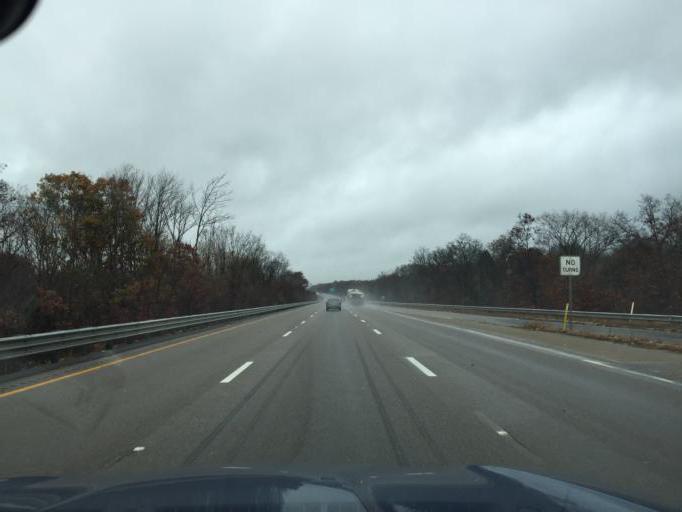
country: US
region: Massachusetts
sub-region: Bristol County
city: Attleboro
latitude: 41.9358
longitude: -71.3176
